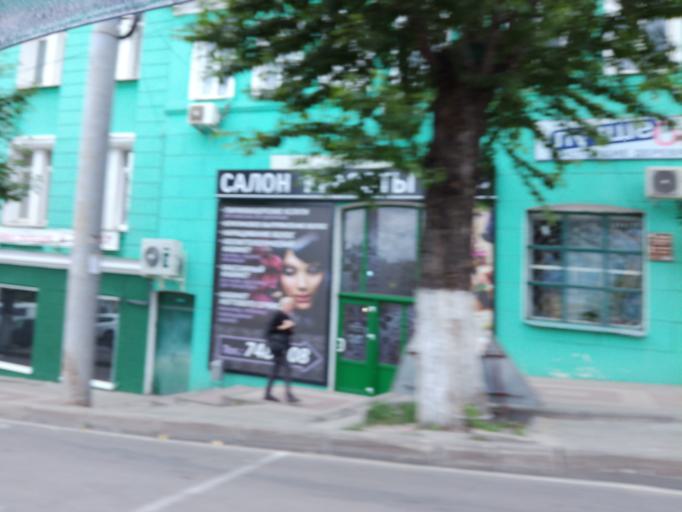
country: RU
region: Kursk
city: Kursk
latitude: 51.7290
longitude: 36.1901
